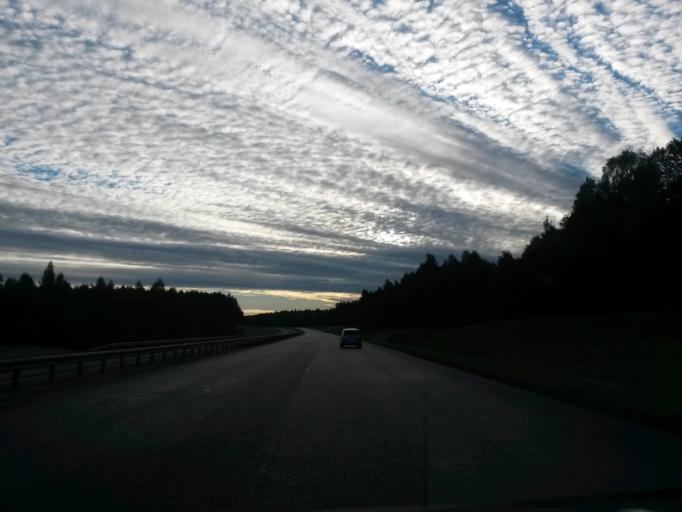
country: RU
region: Vladimir
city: Arsaki
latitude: 56.5139
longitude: 38.5412
